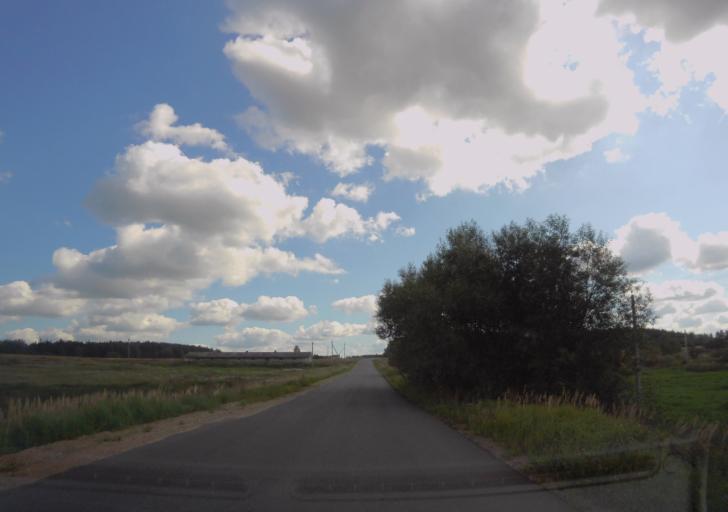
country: BY
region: Minsk
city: Horad Barysaw
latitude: 54.4103
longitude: 28.4602
